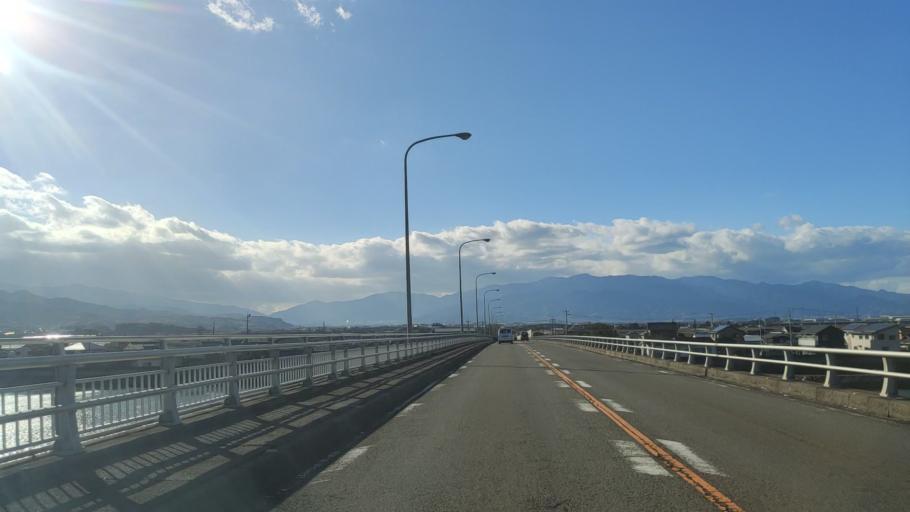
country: JP
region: Ehime
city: Saijo
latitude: 33.9177
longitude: 133.1519
